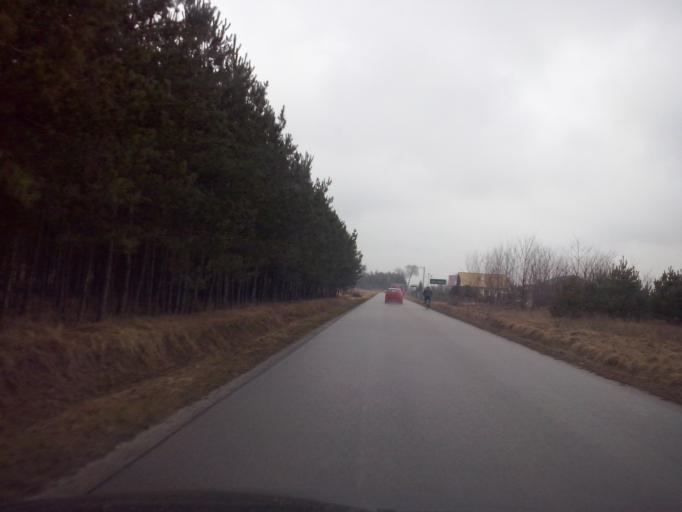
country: PL
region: Subcarpathian Voivodeship
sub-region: Powiat nizanski
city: Bieliny
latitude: 50.4588
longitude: 22.2834
